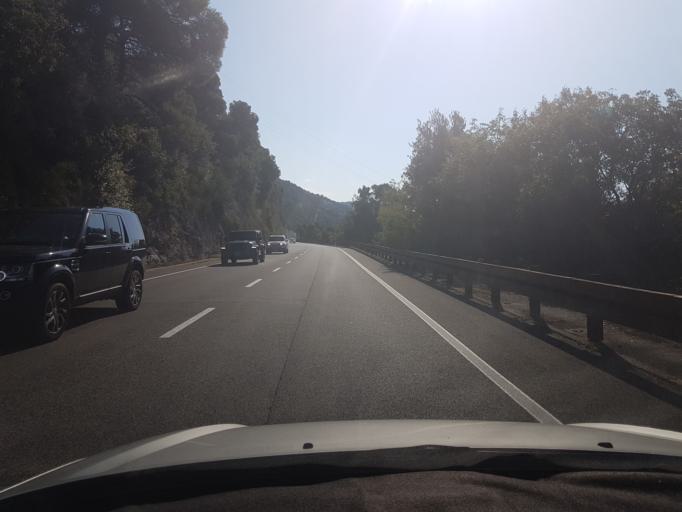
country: IT
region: Friuli Venezia Giulia
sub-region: Provincia di Trieste
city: Aurisina
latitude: 45.7427
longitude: 13.6686
